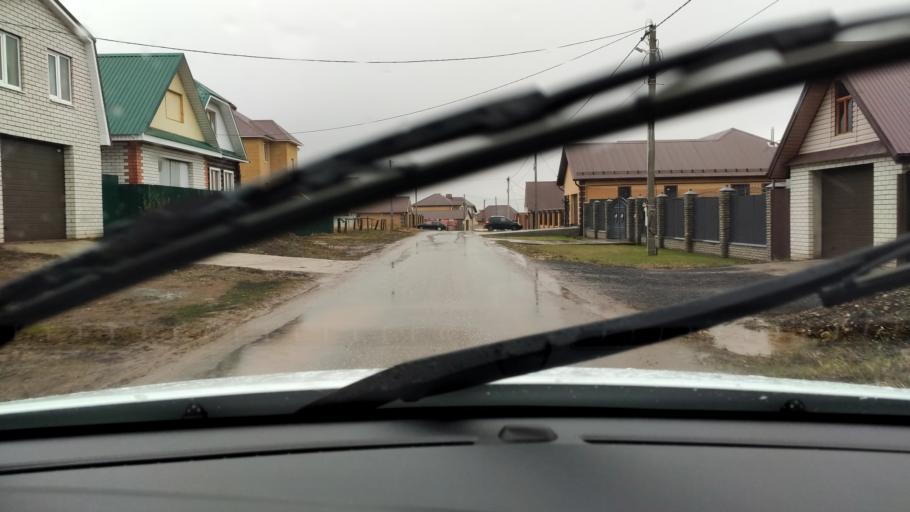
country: RU
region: Tatarstan
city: Vysokaya Gora
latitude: 55.9033
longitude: 49.3208
